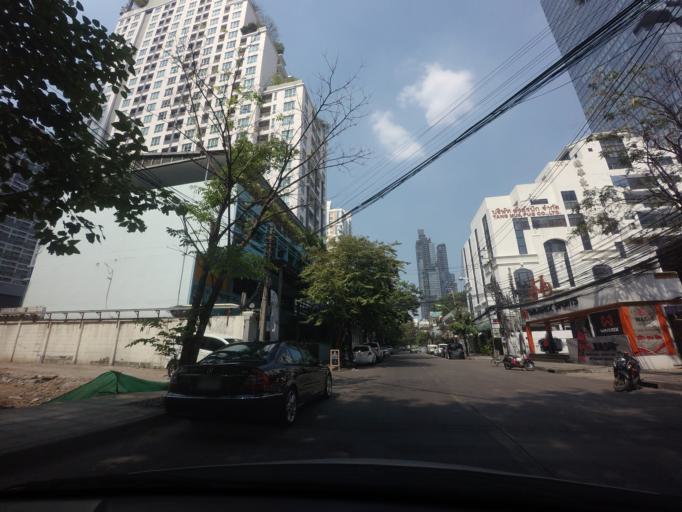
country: TH
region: Bangkok
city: Bang Rak
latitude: 13.7223
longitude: 100.5276
